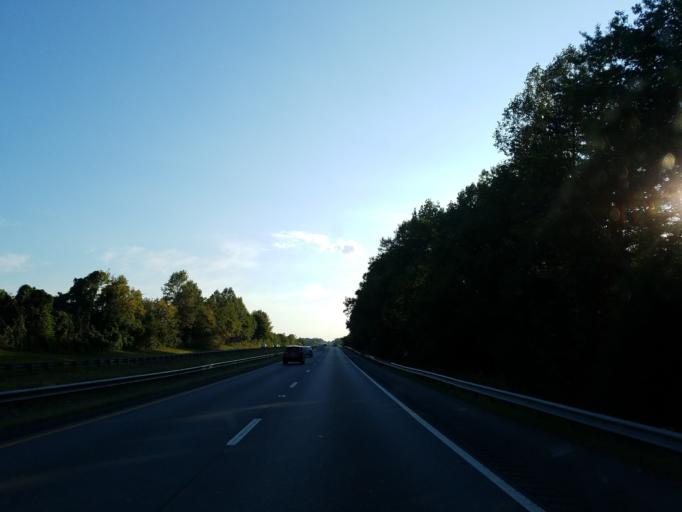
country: US
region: North Carolina
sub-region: Cleveland County
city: Kings Mountain
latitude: 35.2178
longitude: -81.3442
